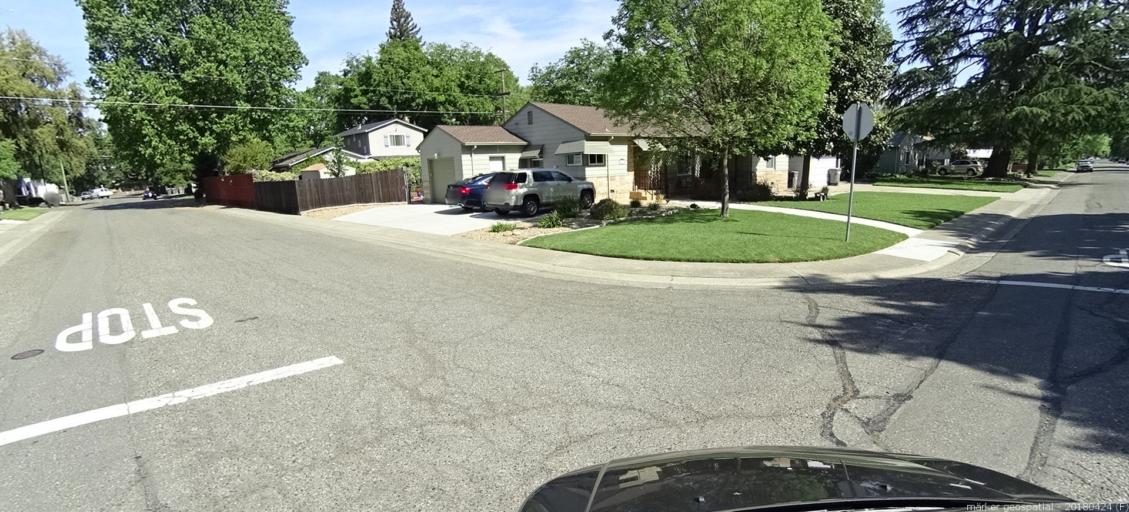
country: US
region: California
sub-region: Yolo County
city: West Sacramento
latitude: 38.5659
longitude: -121.5324
